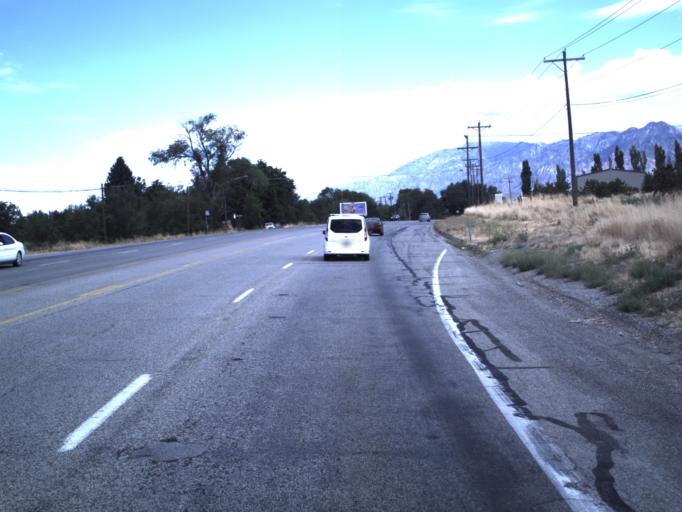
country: US
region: Utah
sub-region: Box Elder County
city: Perry
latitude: 41.4541
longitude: -112.0386
